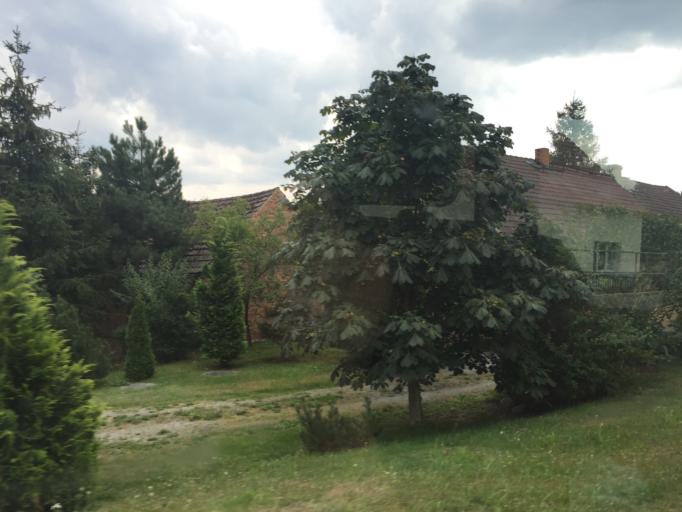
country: DE
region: Saxony
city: Schleife
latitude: 51.4996
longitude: 14.5197
